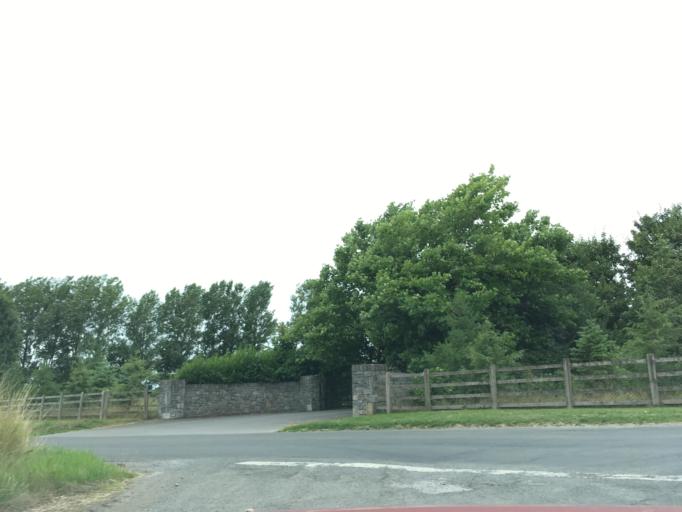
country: IE
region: Munster
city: Cashel
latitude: 52.4796
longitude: -7.9098
